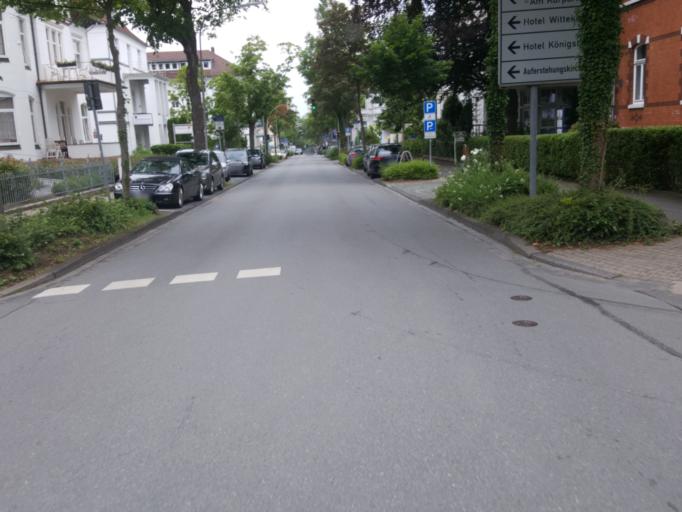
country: DE
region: North Rhine-Westphalia
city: Bad Oeynhausen
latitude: 52.2024
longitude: 8.7997
